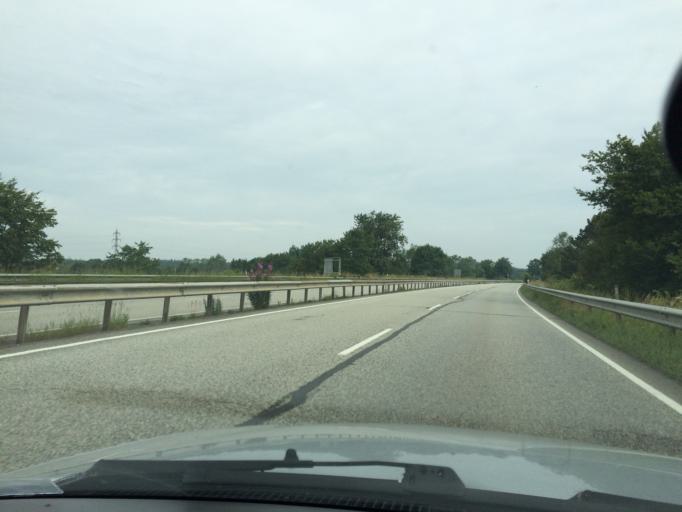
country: DE
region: Schleswig-Holstein
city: Harrislee
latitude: 54.7804
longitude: 9.4063
